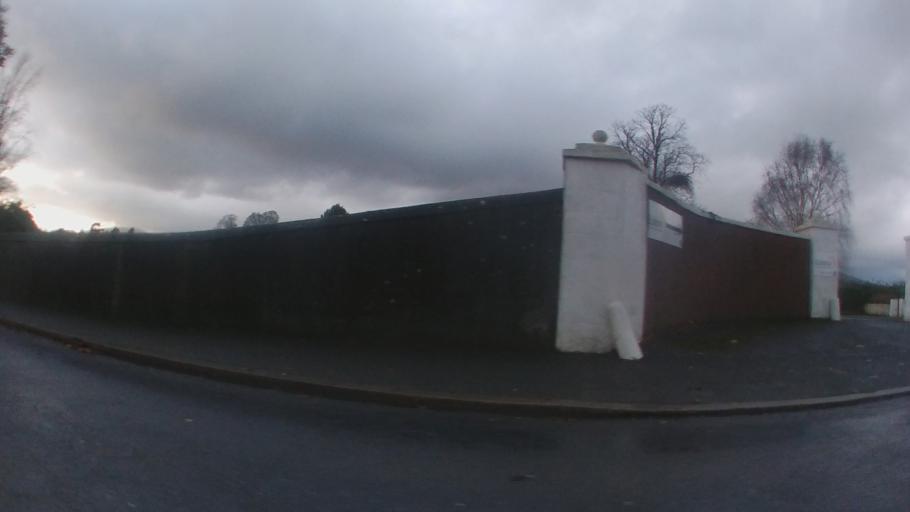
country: IE
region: Leinster
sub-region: Wicklow
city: Kilcoole
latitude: 53.1138
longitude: -6.0658
